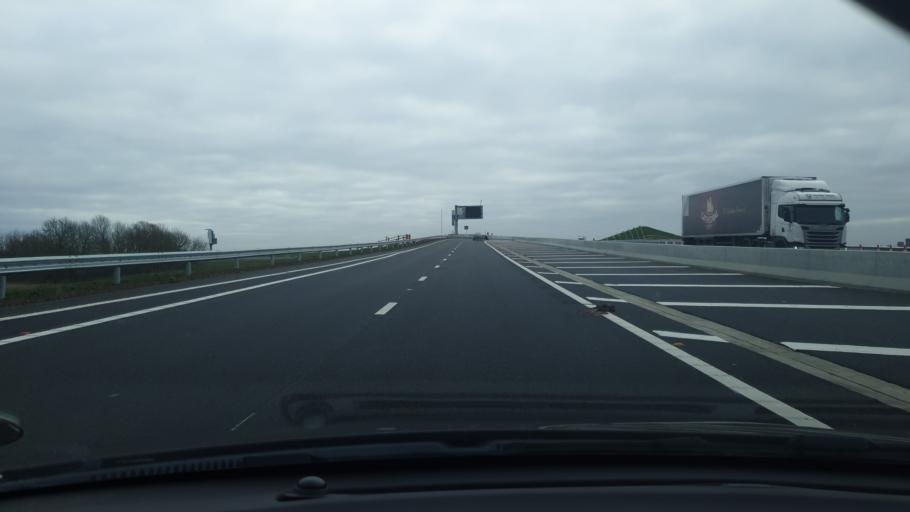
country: GB
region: England
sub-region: Cambridgeshire
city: Brampton
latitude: 52.3302
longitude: -0.2530
